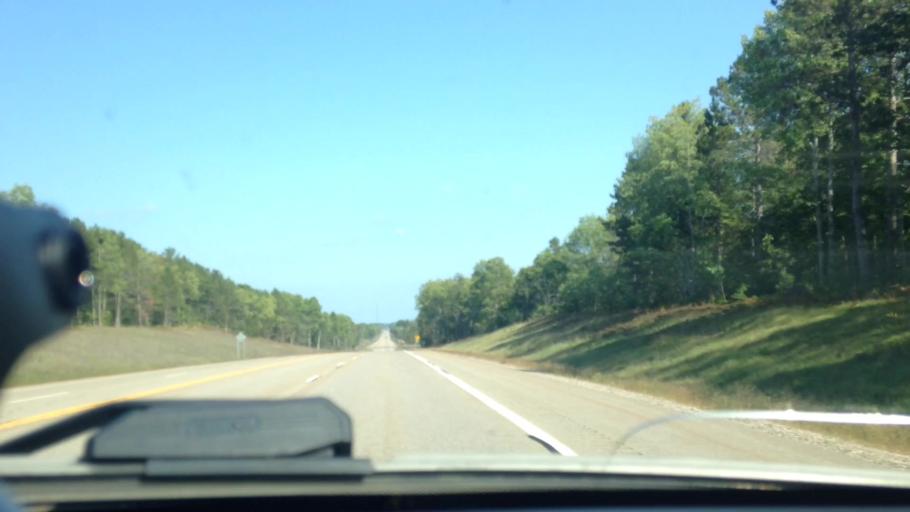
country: US
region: Michigan
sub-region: Chippewa County
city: Sault Ste. Marie
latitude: 46.3635
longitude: -84.7689
